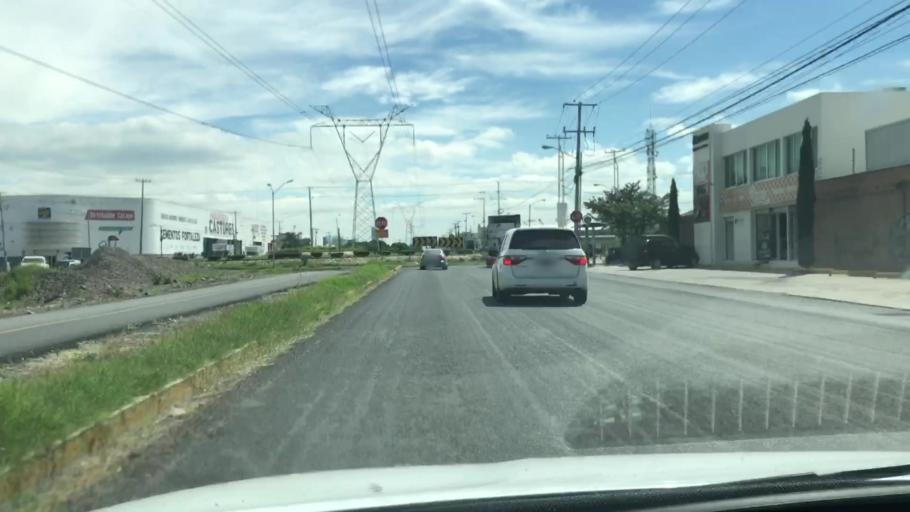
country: MX
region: Guanajuato
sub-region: Celaya
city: La Trinidad
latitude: 20.5506
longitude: -100.8043
